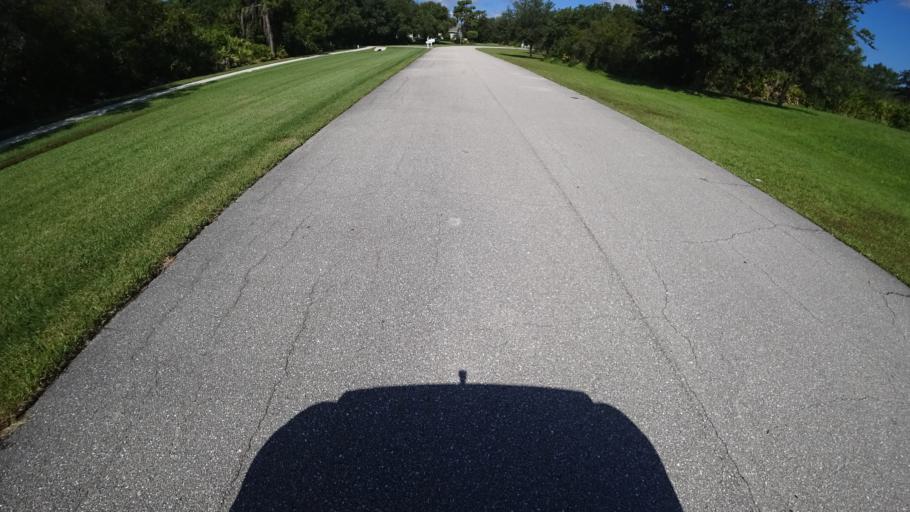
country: US
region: Florida
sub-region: Sarasota County
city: Fruitville
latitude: 27.3900
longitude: -82.3033
